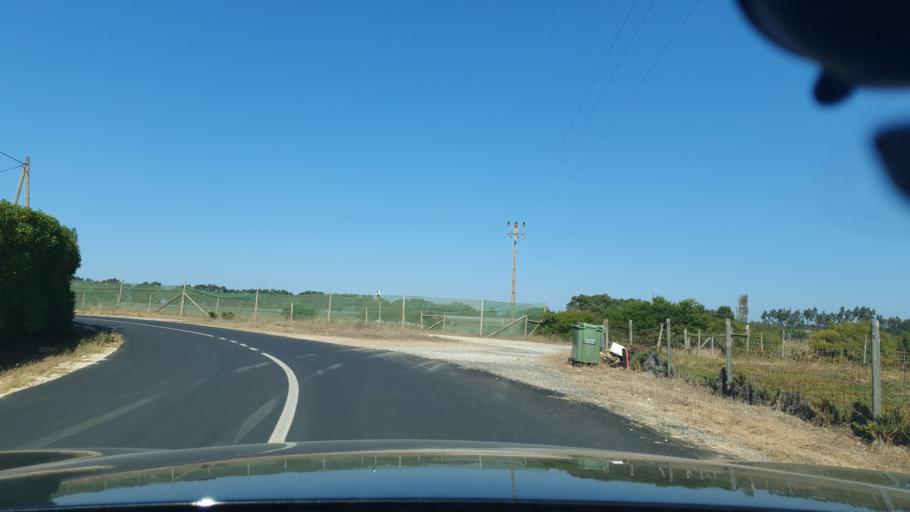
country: PT
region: Beja
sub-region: Odemira
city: Sao Teotonio
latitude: 37.4652
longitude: -8.7899
